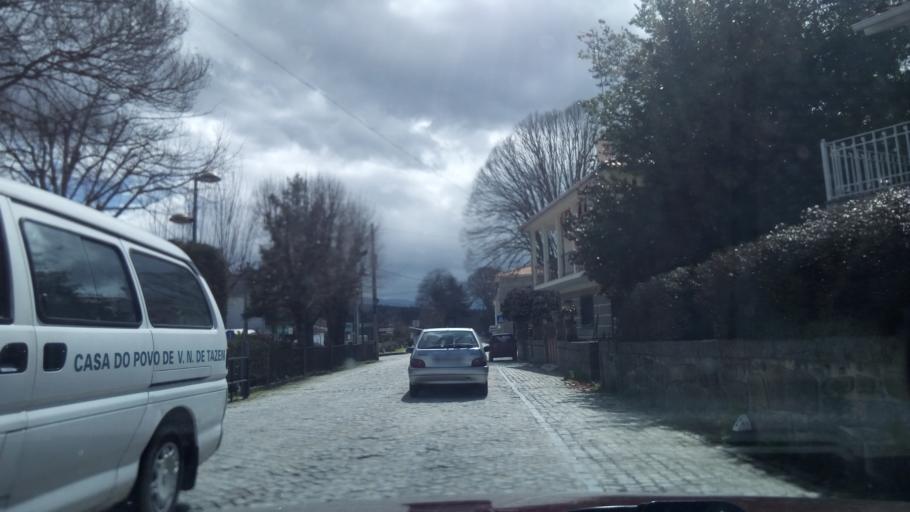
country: PT
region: Guarda
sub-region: Fornos de Algodres
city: Fornos de Algodres
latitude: 40.5874
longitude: -7.5393
